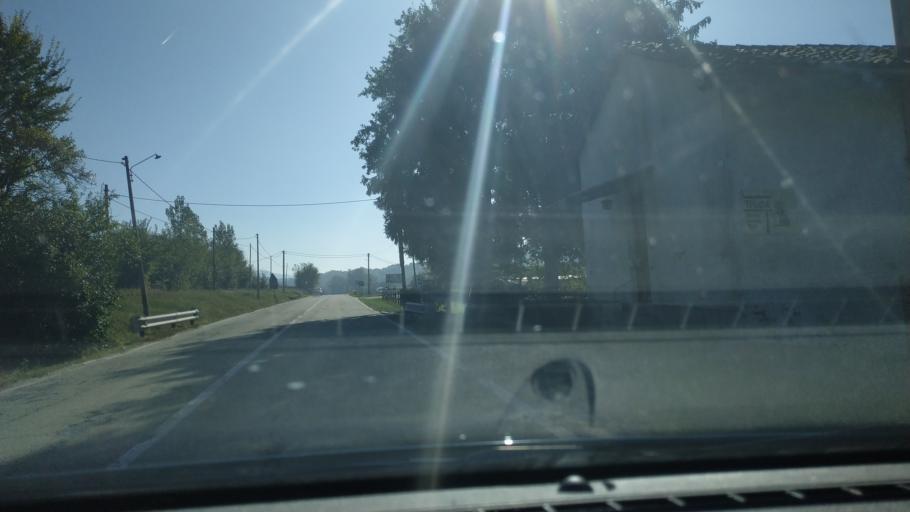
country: IT
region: Piedmont
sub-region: Provincia di Asti
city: Robella
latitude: 45.0881
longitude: 8.1022
